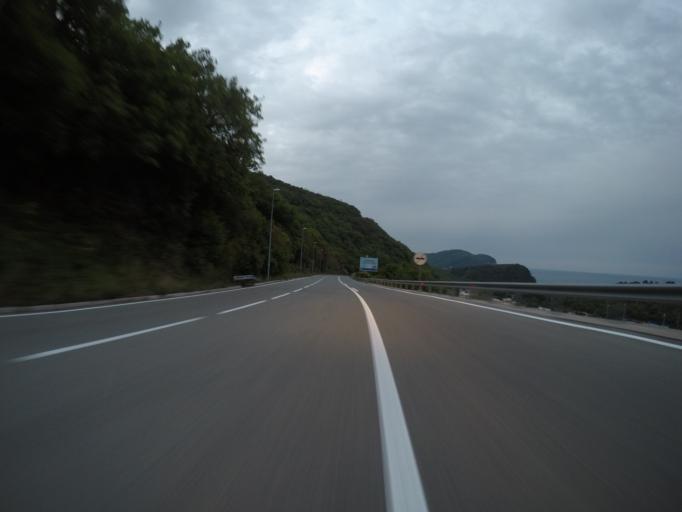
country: ME
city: Petrovac na Moru
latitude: 42.2094
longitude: 18.9464
